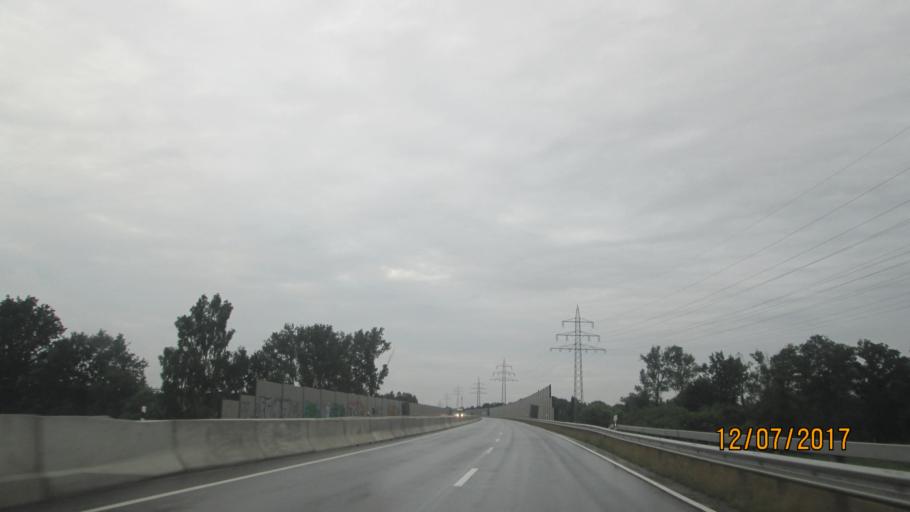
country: DE
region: Lower Saxony
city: Gifhorn
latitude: 52.4737
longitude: 10.5244
